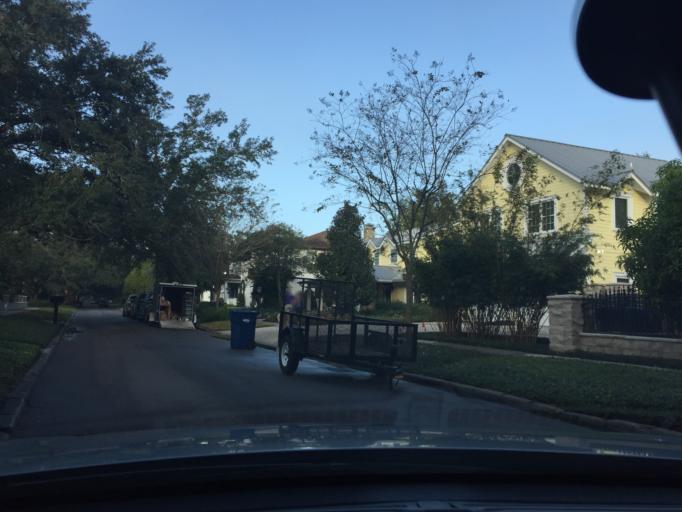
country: US
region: Florida
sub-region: Hillsborough County
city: Tampa
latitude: 27.9368
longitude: -82.4883
